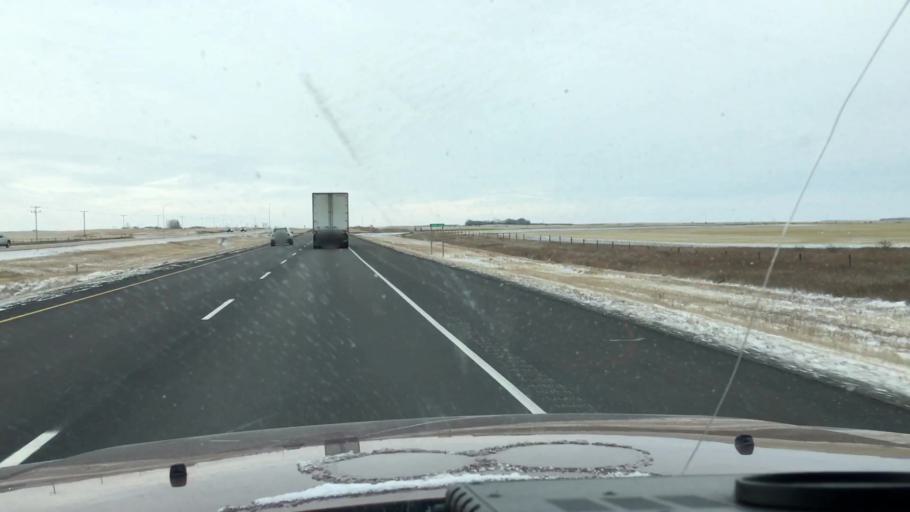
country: CA
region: Saskatchewan
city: Saskatoon
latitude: 51.7968
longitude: -106.4875
